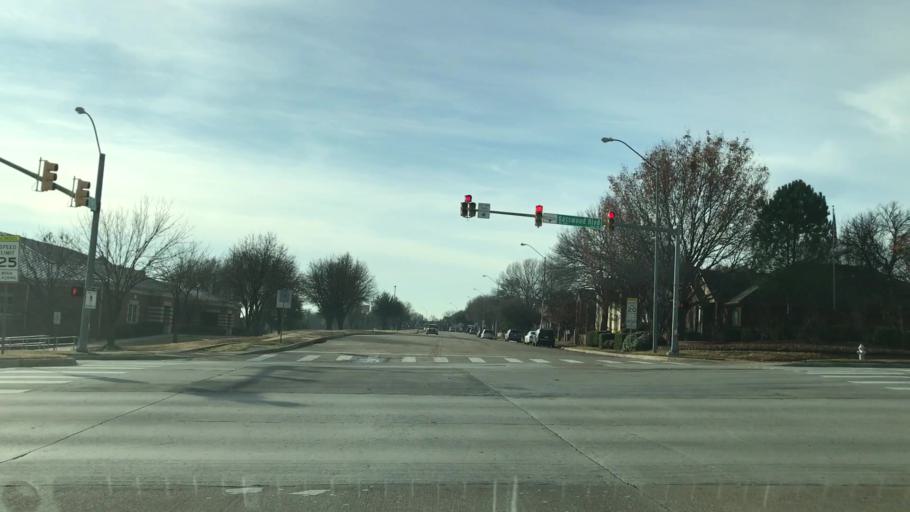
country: US
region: Texas
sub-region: Tarrant County
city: Watauga
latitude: 32.8717
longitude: -97.2784
